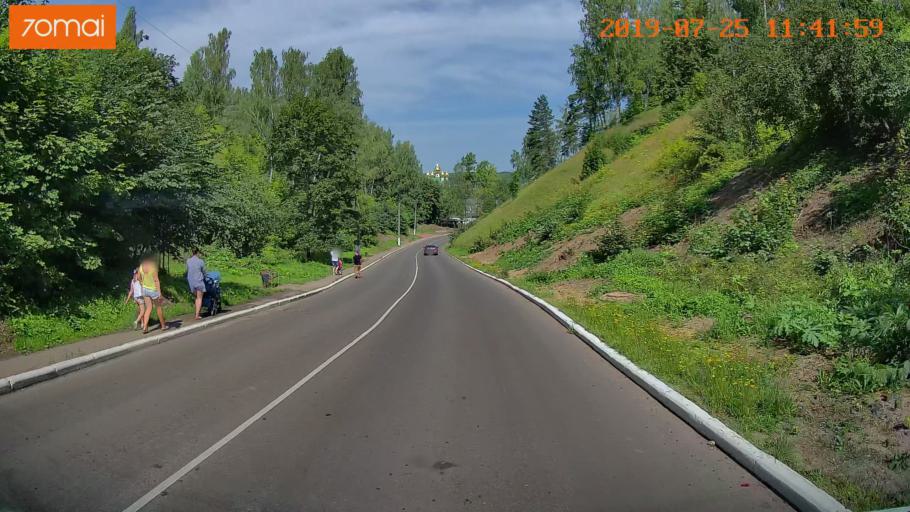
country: RU
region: Ivanovo
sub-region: Privolzhskiy Rayon
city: Ples
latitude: 57.4581
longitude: 41.5119
